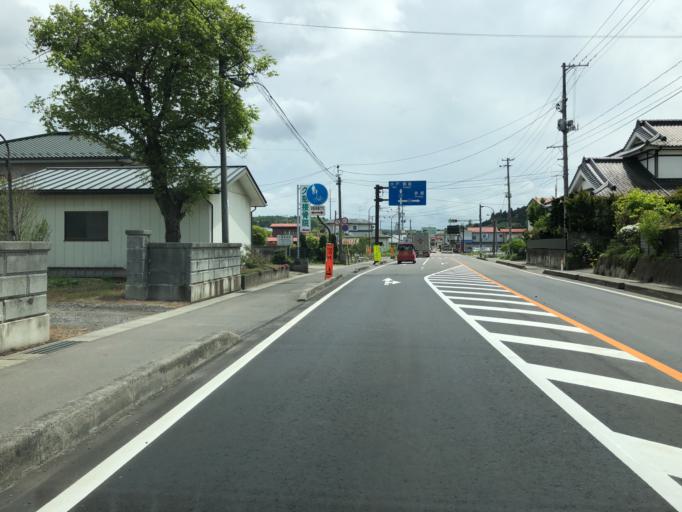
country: JP
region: Fukushima
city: Ishikawa
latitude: 37.1038
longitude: 140.3482
